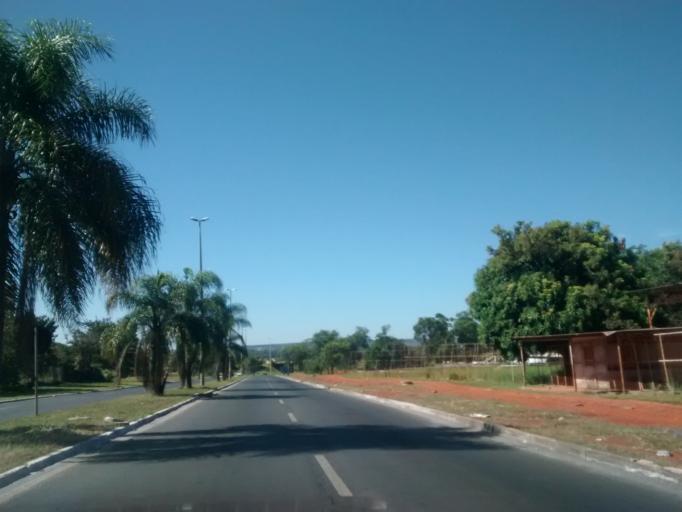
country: BR
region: Federal District
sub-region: Brasilia
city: Brasilia
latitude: -15.8285
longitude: -47.9033
